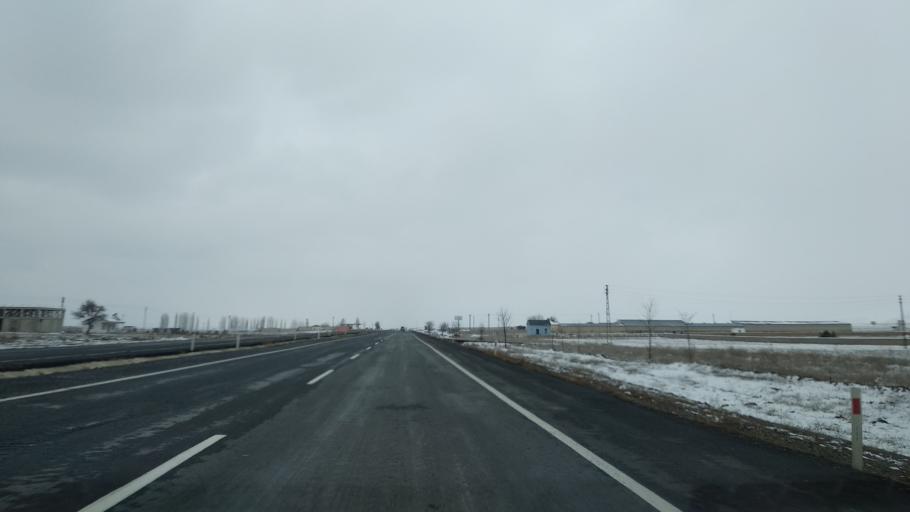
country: TR
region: Kayseri
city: Elbasi
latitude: 38.6442
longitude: 35.9460
